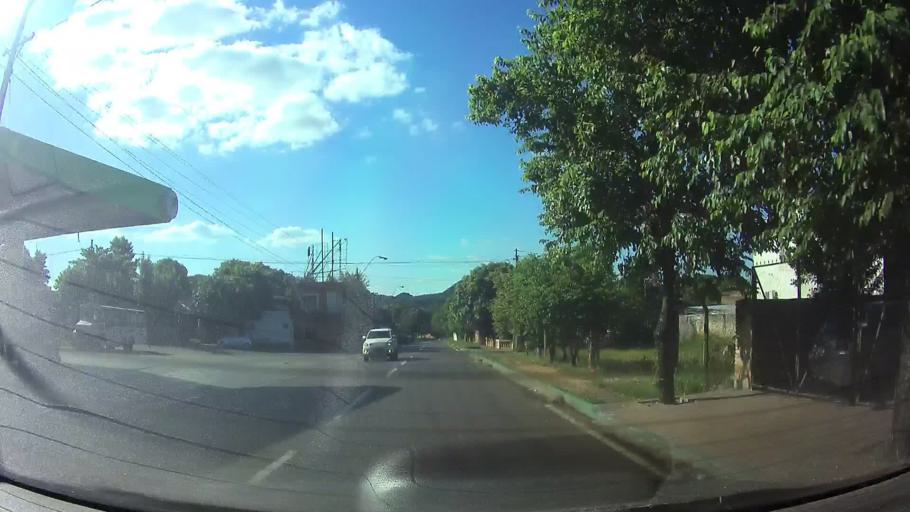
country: PY
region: Cordillera
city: Caacupe
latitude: -25.3914
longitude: -57.1470
